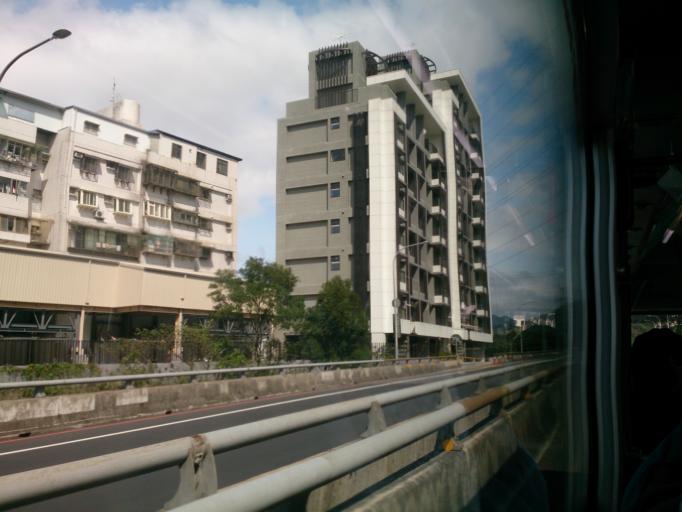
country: TW
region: Taipei
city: Taipei
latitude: 24.9996
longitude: 121.6190
